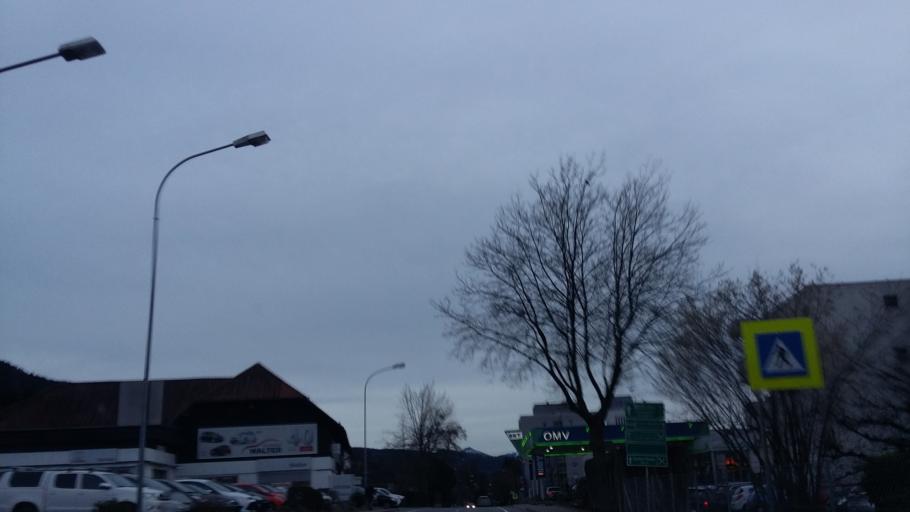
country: AT
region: Vorarlberg
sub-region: Politischer Bezirk Bregenz
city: Lochau
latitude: 47.5354
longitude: 9.7522
